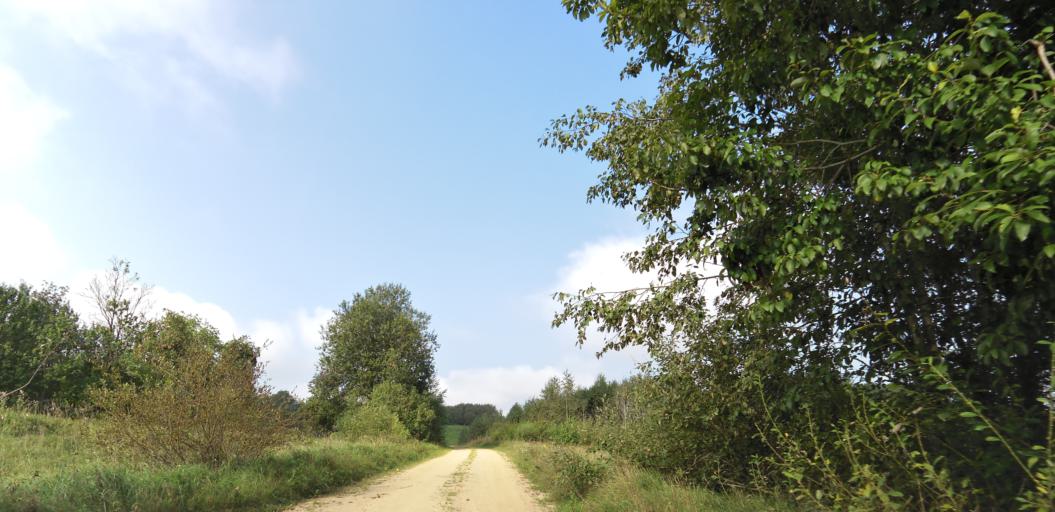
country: LT
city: Grigiskes
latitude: 54.7721
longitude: 25.0652
